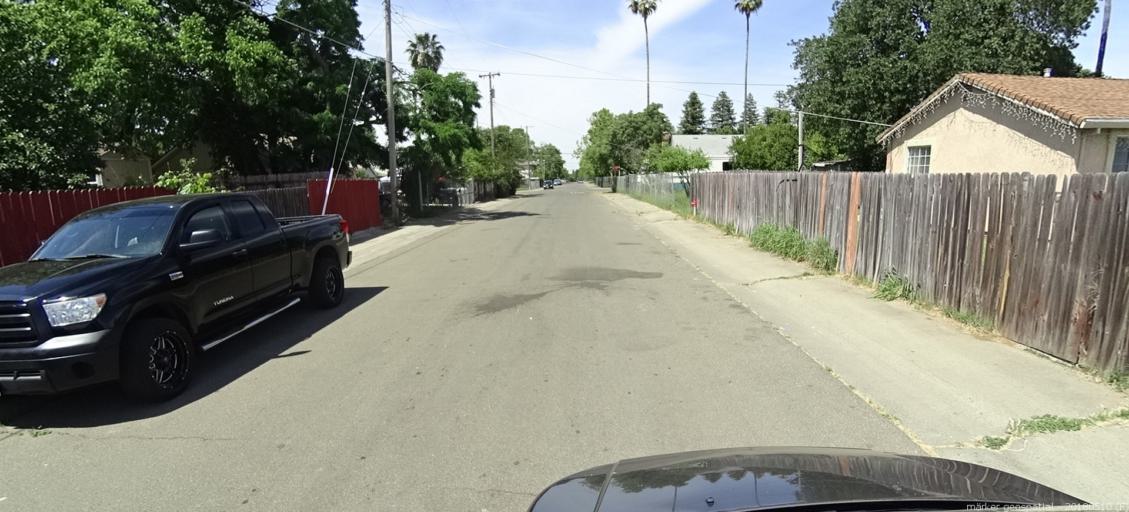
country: US
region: California
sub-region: Sacramento County
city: Rio Linda
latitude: 38.6340
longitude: -121.4503
